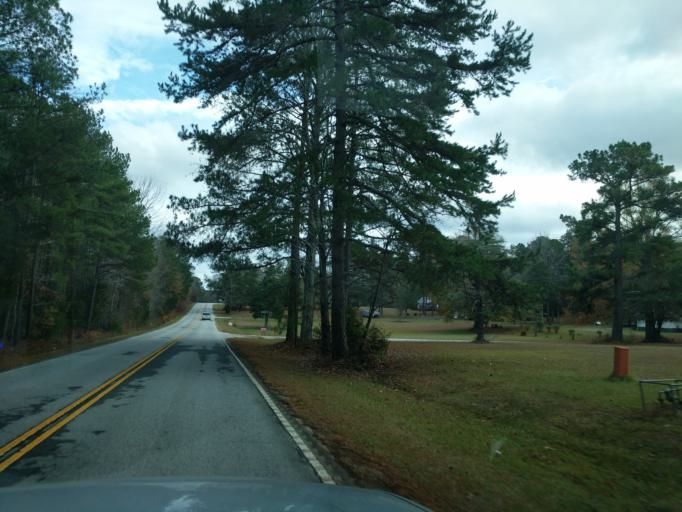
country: US
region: South Carolina
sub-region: Greenwood County
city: Ware Shoals
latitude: 34.4020
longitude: -82.2019
